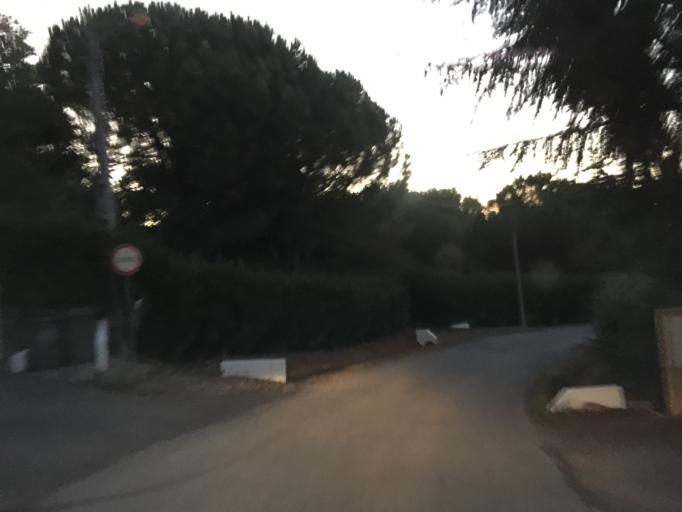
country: PT
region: Portalegre
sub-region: Castelo de Vide
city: Castelo de Vide
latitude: 39.4047
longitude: -7.4453
